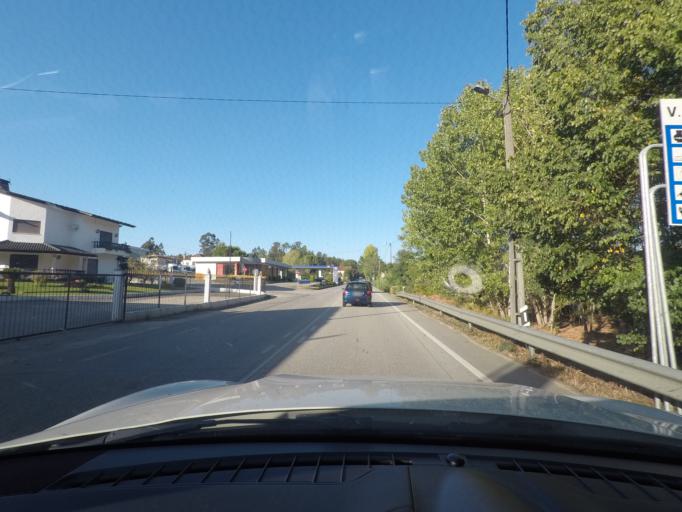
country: PT
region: Coimbra
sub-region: Vila Nova de Poiares
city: Poiares
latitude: 40.1841
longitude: -8.2600
